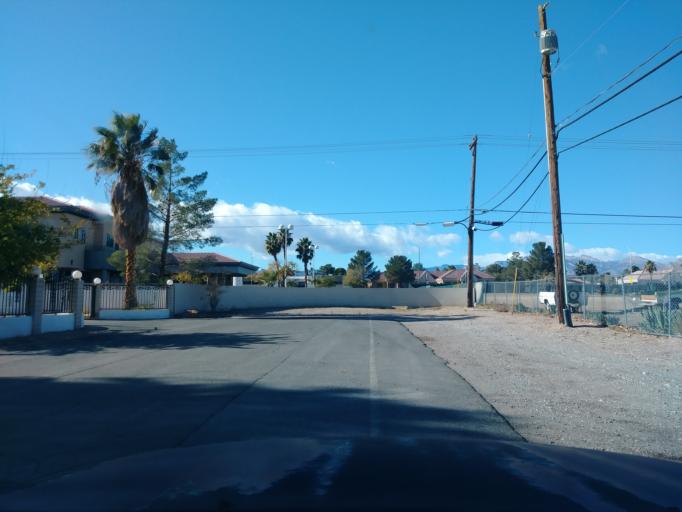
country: US
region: Nevada
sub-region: Clark County
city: Spring Valley
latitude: 36.1499
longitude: -115.2241
